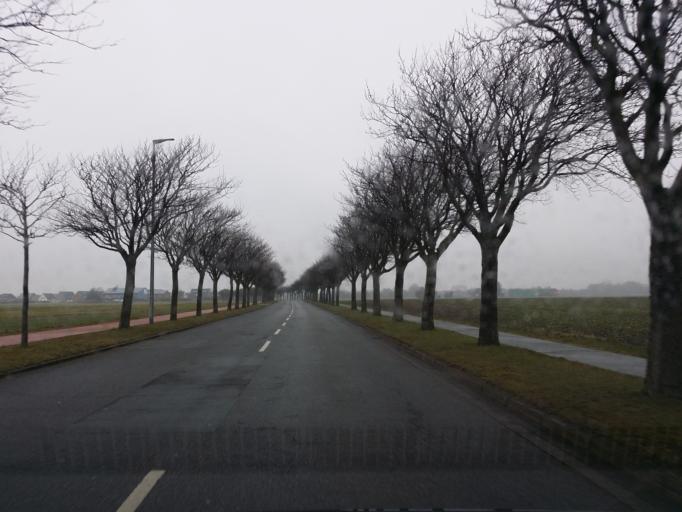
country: DE
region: Schleswig-Holstein
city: Burg auf Fehmarn
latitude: 54.4243
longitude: 11.2060
